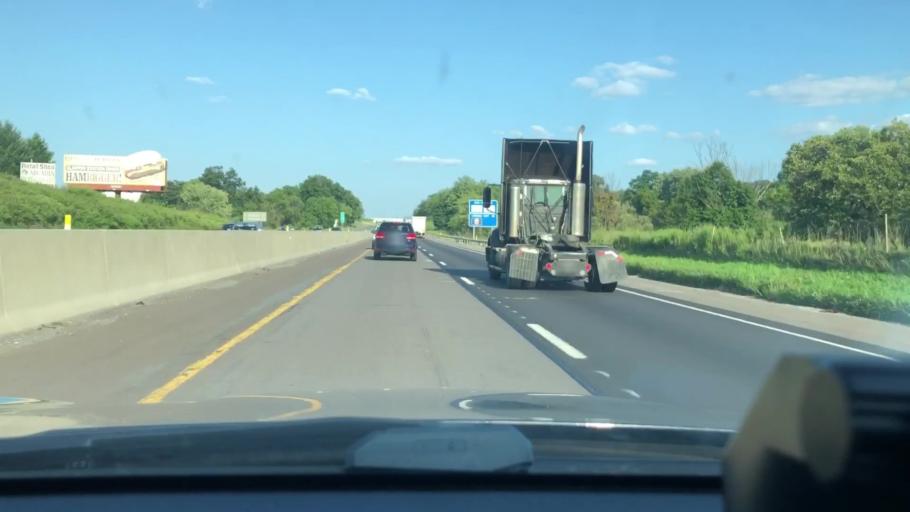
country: US
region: Pennsylvania
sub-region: Berks County
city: Topton
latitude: 40.5810
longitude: -75.7192
